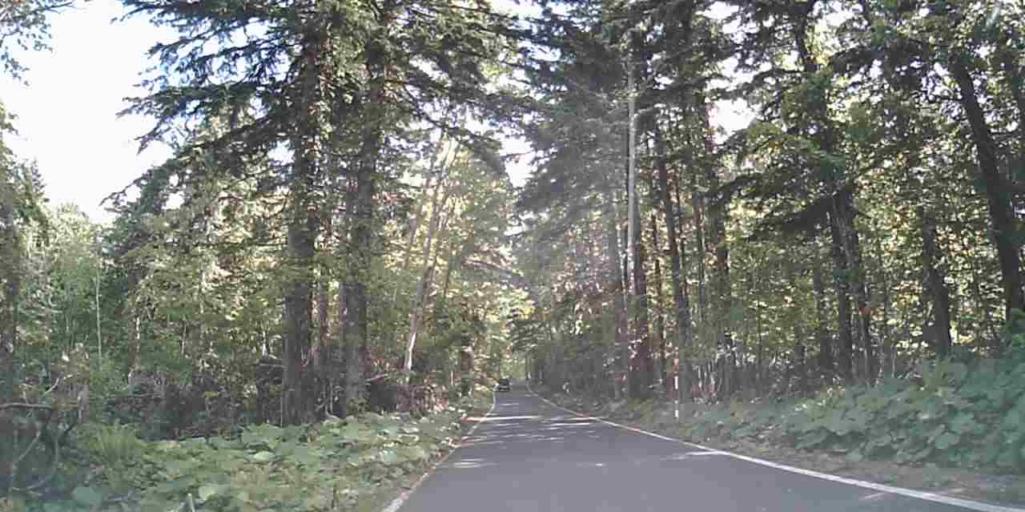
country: JP
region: Hokkaido
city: Shiraoi
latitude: 42.7374
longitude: 141.4110
